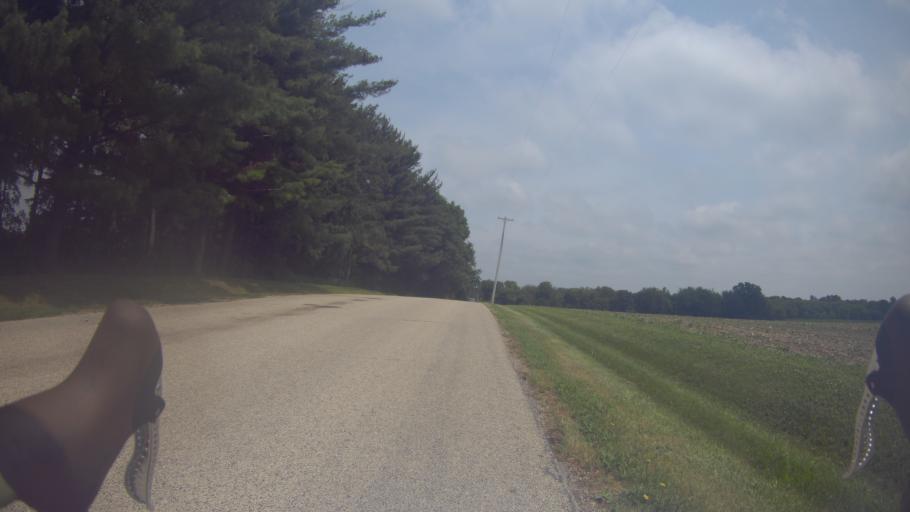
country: US
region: Wisconsin
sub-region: Jefferson County
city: Lake Ripley
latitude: 42.9845
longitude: -88.9986
